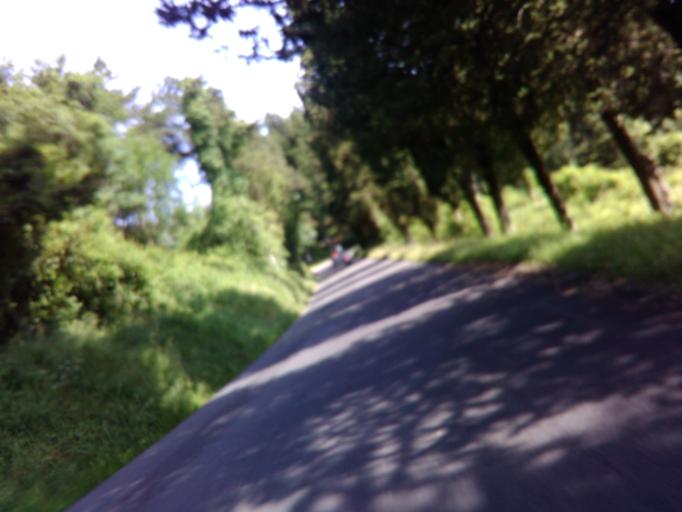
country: IT
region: Tuscany
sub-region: Provincia di Massa-Carrara
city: Fosdinovo
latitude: 44.1425
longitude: 10.0220
